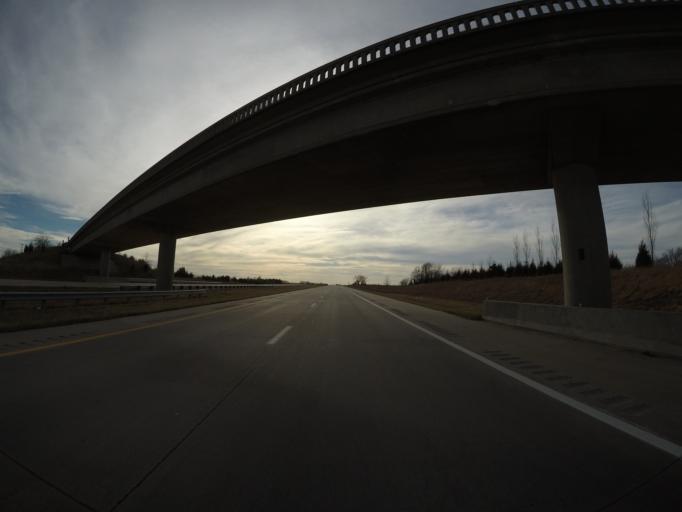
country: US
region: Kansas
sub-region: Franklin County
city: Wellsville
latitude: 38.6852
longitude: -95.1211
